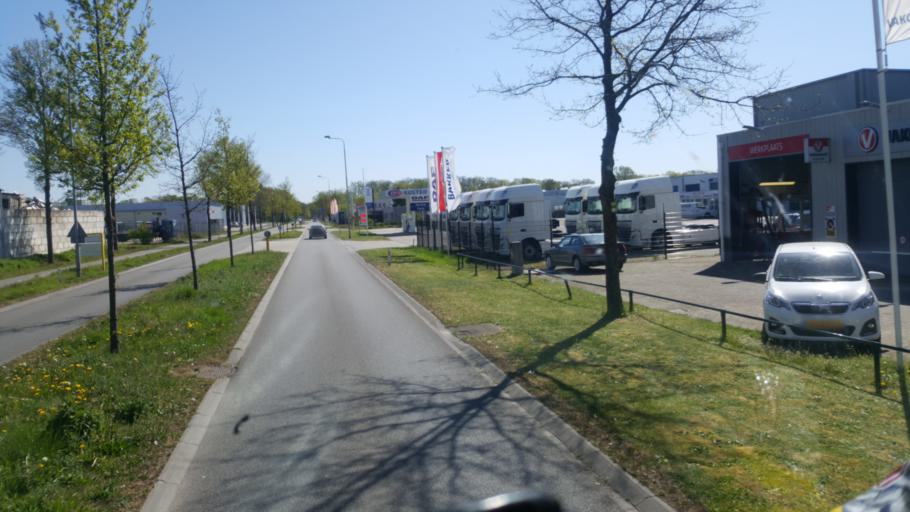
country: NL
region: Gelderland
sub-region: Gemeente Winterswijk
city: Winterswijk
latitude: 51.9612
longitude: 6.7135
